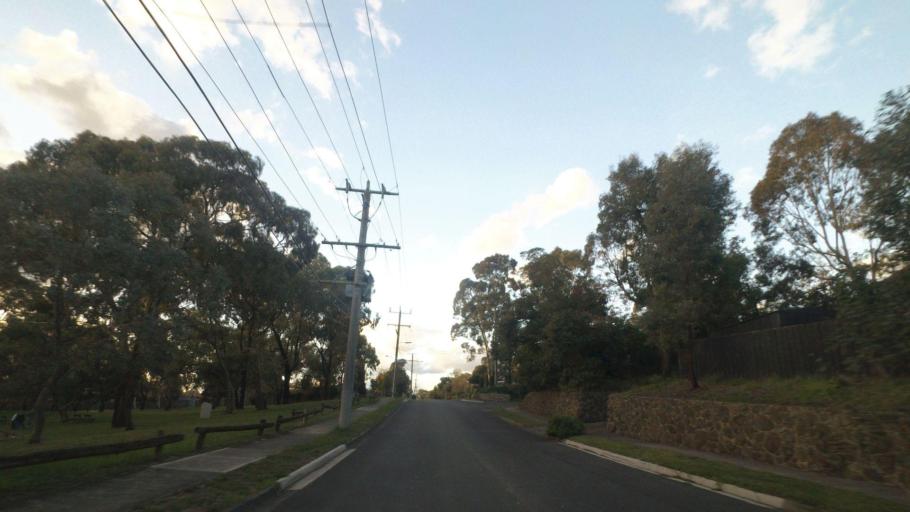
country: AU
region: Victoria
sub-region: Banyule
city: Lower Plenty
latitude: -37.7267
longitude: 145.1182
